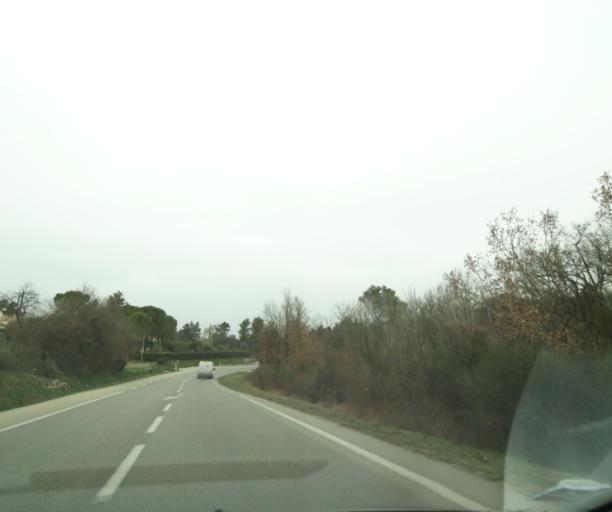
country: FR
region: Provence-Alpes-Cote d'Azur
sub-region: Departement des Bouches-du-Rhone
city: Fuveau
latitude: 43.4624
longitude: 5.5468
